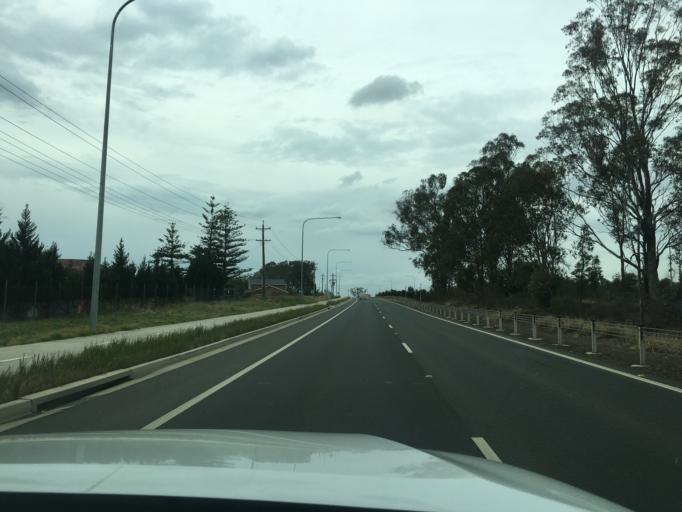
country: AU
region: New South Wales
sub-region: Campbelltown Municipality
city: Denham Court
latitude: -33.9785
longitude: 150.8055
